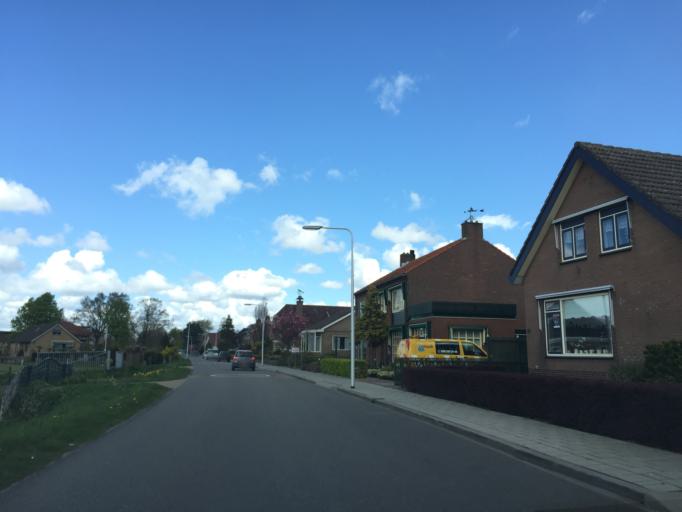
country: NL
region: South Holland
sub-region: Gemeente Kaag en Braassem
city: Oude Wetering
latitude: 52.2069
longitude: 4.6170
